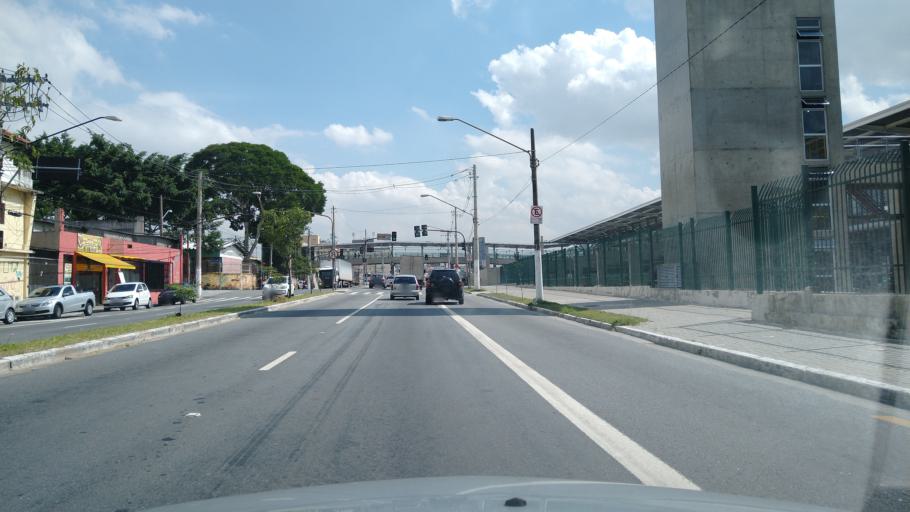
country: BR
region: Sao Paulo
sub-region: Guarulhos
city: Guarulhos
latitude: -23.4981
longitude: -46.5190
